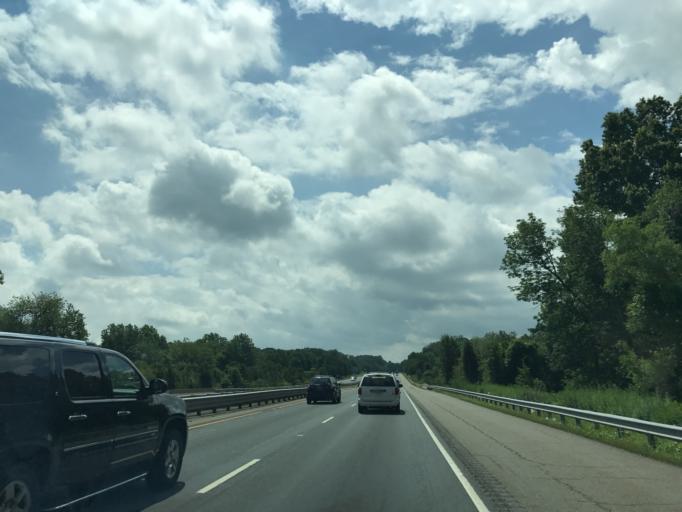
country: US
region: New Jersey
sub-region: Morris County
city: Madison
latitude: 40.7827
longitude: -74.4161
